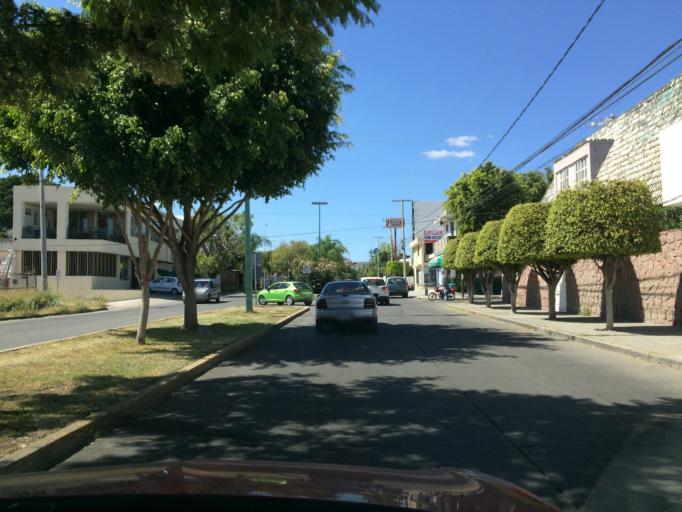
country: MX
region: Guanajuato
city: Leon
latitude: 21.1190
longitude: -101.6975
